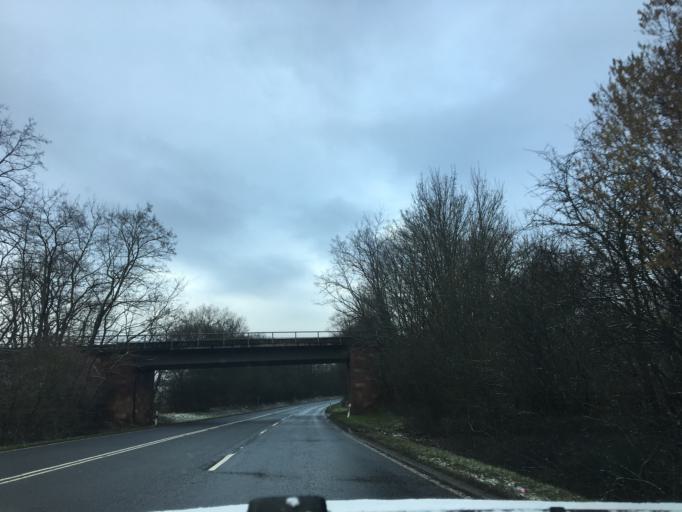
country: DE
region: Rheinland-Pfalz
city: Kirchheimbolanden
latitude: 49.6781
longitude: 8.0119
